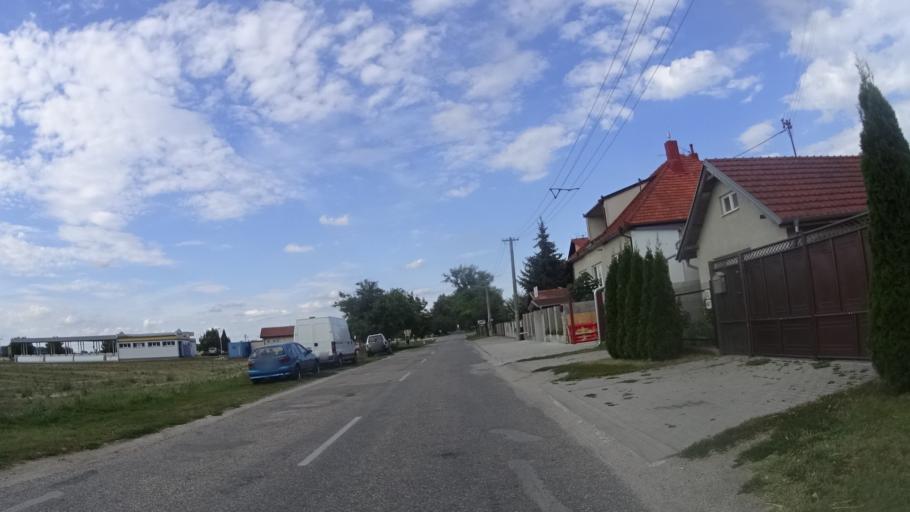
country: SK
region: Trnavsky
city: Gabcikovo
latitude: 47.9098
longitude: 17.5266
